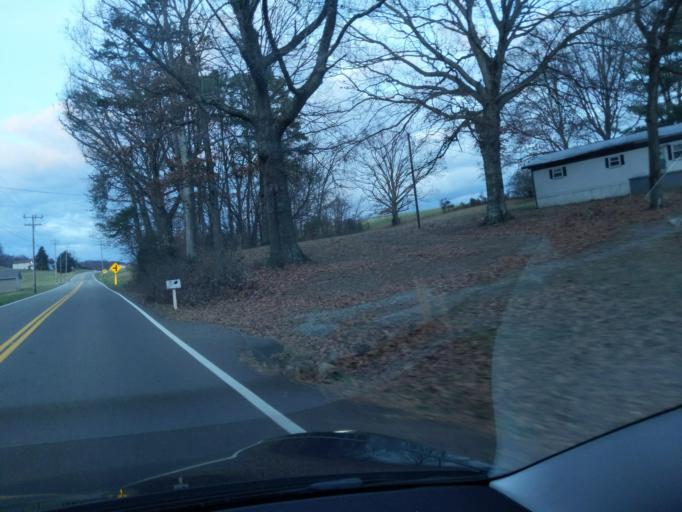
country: US
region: Tennessee
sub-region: Jefferson County
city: White Pine
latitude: 36.1072
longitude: -83.3484
